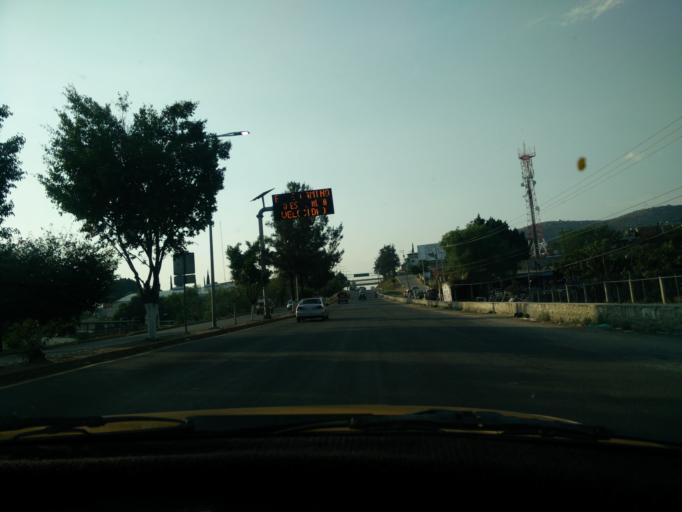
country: MX
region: Oaxaca
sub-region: Santa Maria Atzompa
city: San Jeronimo Yahuiche
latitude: 17.0942
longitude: -96.7485
